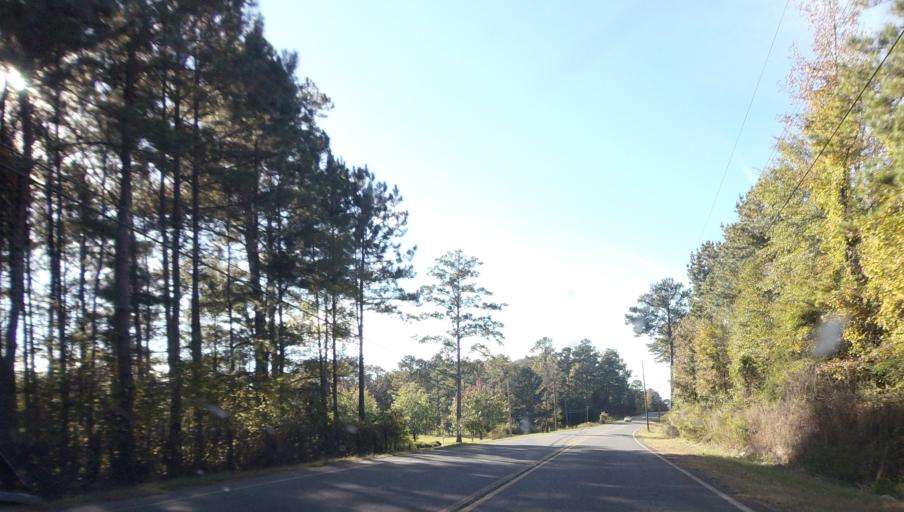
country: US
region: Georgia
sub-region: Talbot County
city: Talbotton
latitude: 32.6782
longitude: -84.5529
